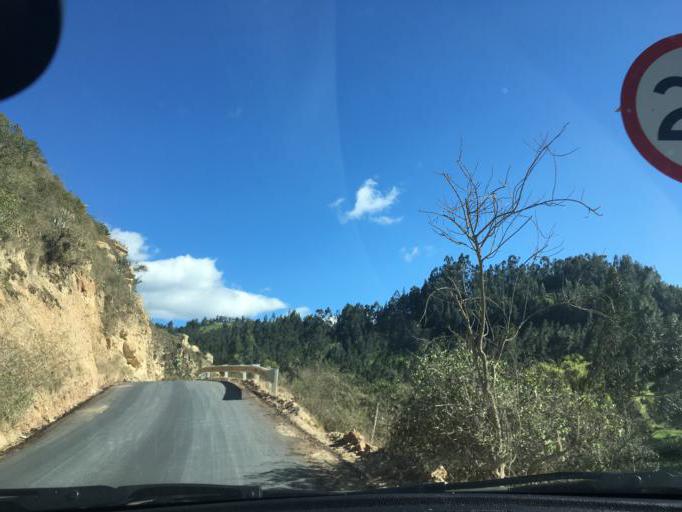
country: CO
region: Boyaca
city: Pesca
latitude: 5.5847
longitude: -72.9727
